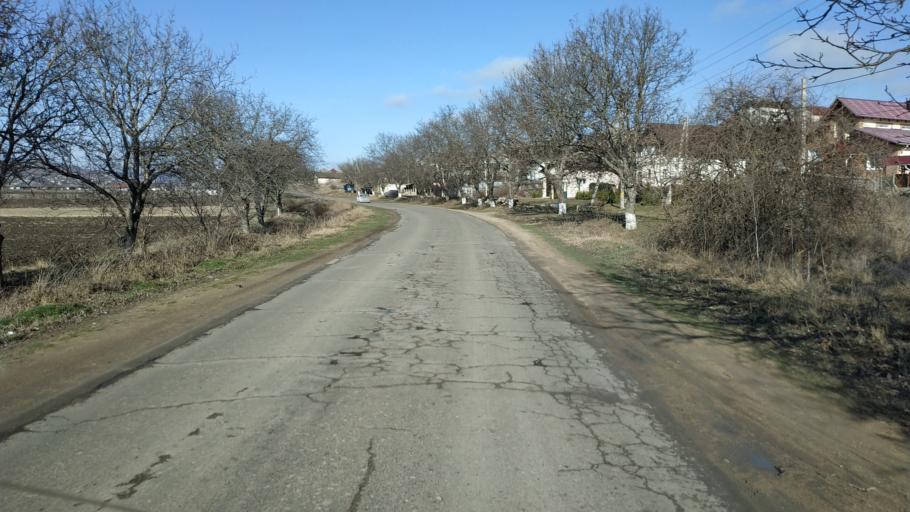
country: MD
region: Laloveni
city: Ialoveni
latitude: 46.9299
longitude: 28.6705
